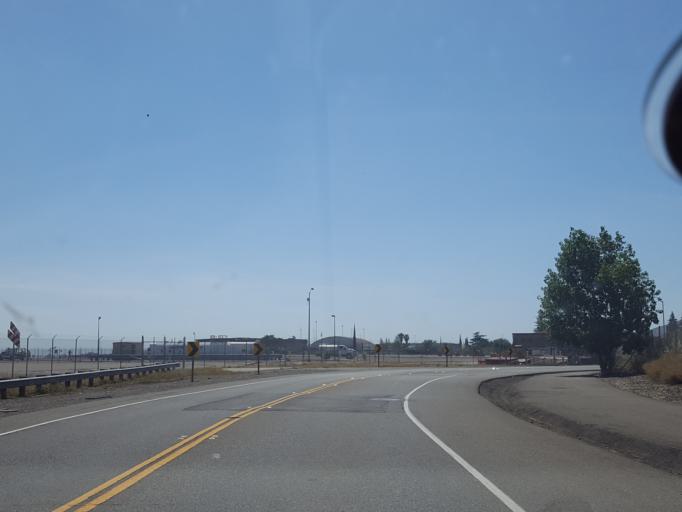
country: US
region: California
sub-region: Sacramento County
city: Rancho Cordova
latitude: 38.5668
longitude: -121.2862
